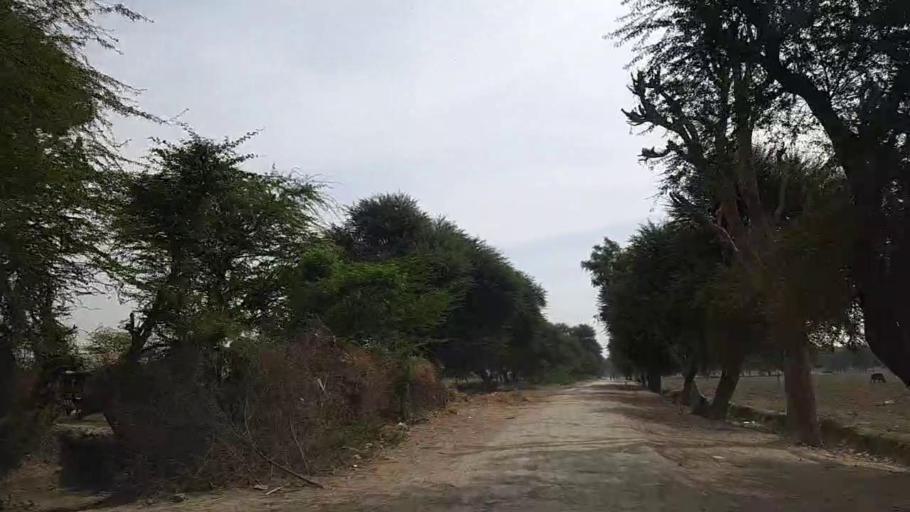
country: PK
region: Sindh
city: Samaro
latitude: 25.2863
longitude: 69.4188
